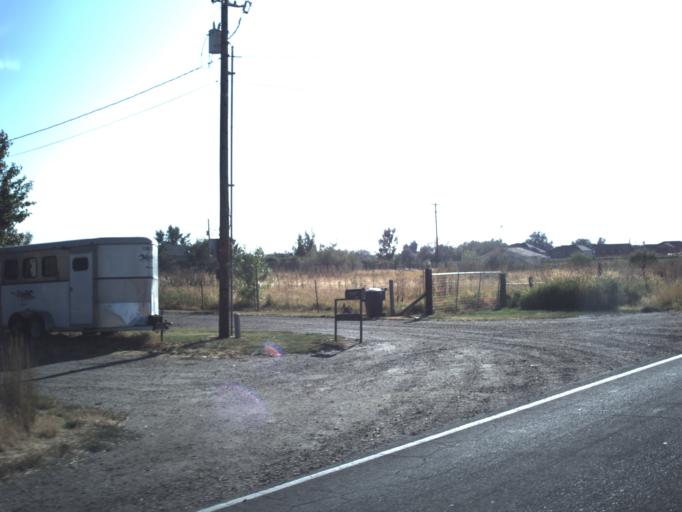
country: US
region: Utah
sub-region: Davis County
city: West Point
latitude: 41.1399
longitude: -112.1038
